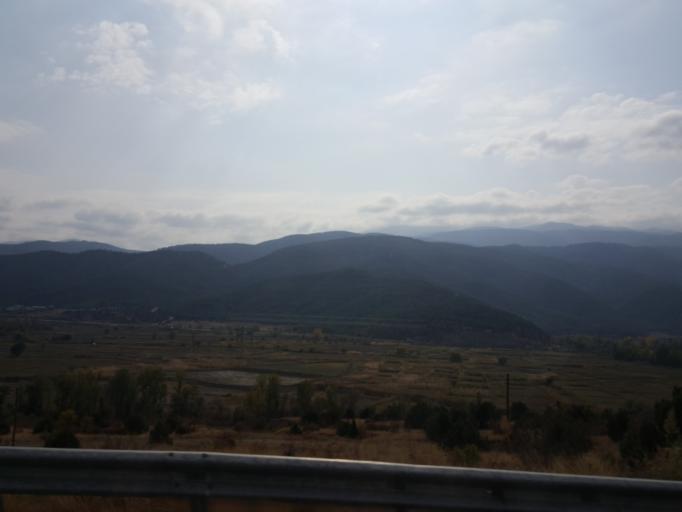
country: TR
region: Corum
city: Hacihamza
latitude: 41.1071
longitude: 34.3831
